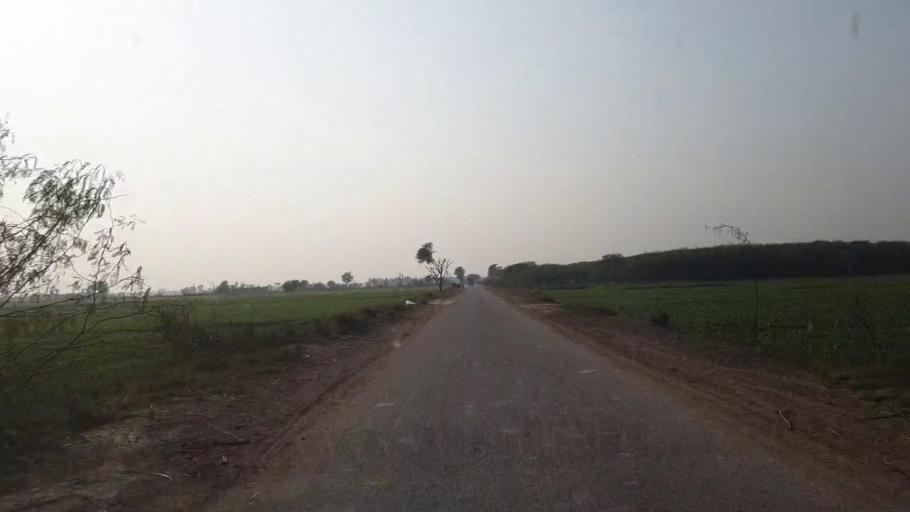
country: PK
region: Sindh
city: Hala
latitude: 25.9147
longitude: 68.4494
